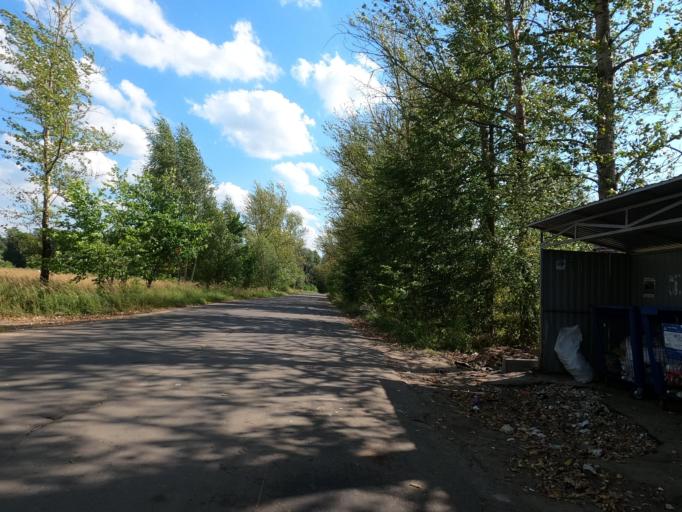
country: RU
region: Moskovskaya
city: Peski
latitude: 55.2245
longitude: 38.7520
